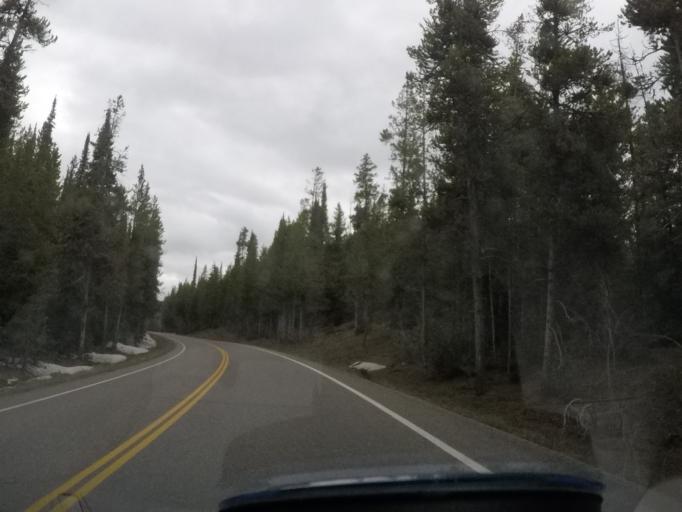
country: US
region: Wyoming
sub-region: Teton County
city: Moose Wilson Road
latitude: 43.9539
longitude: -110.6352
